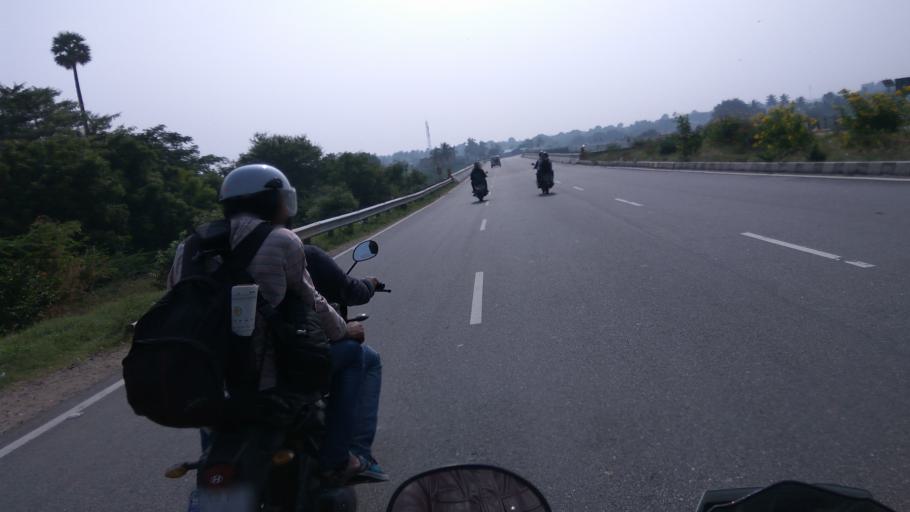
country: IN
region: Tamil Nadu
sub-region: Krishnagiri
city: Krishnagiri
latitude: 12.5992
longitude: 78.1332
